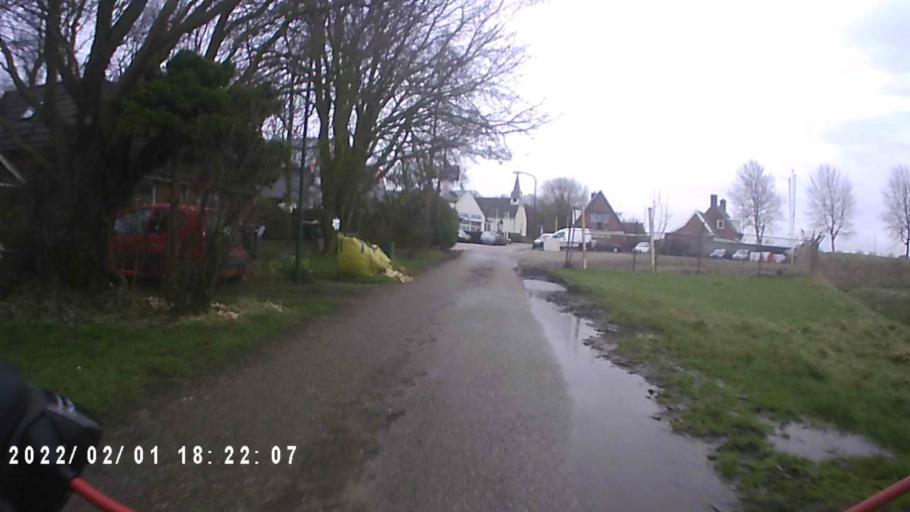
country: NL
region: Groningen
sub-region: Gemeente De Marne
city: Ulrum
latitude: 53.3432
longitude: 6.3285
